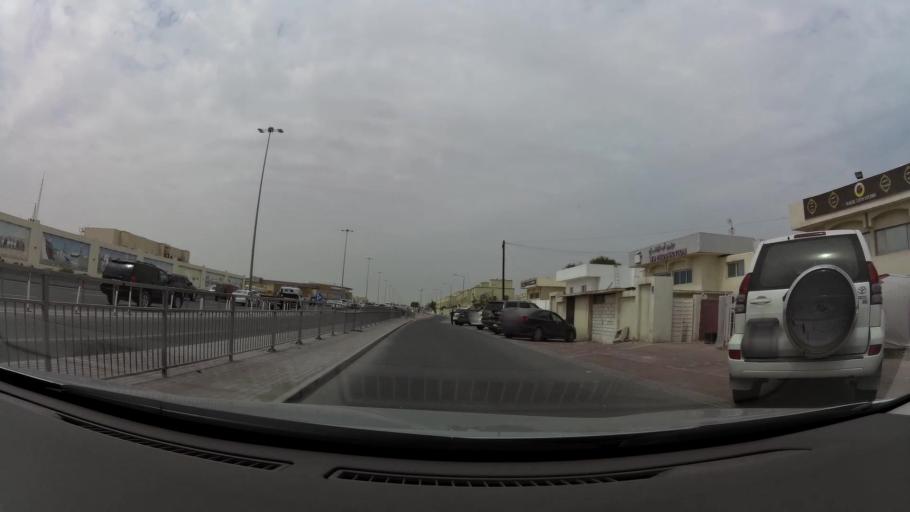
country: QA
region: Baladiyat ar Rayyan
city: Ar Rayyan
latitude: 25.3289
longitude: 51.4660
